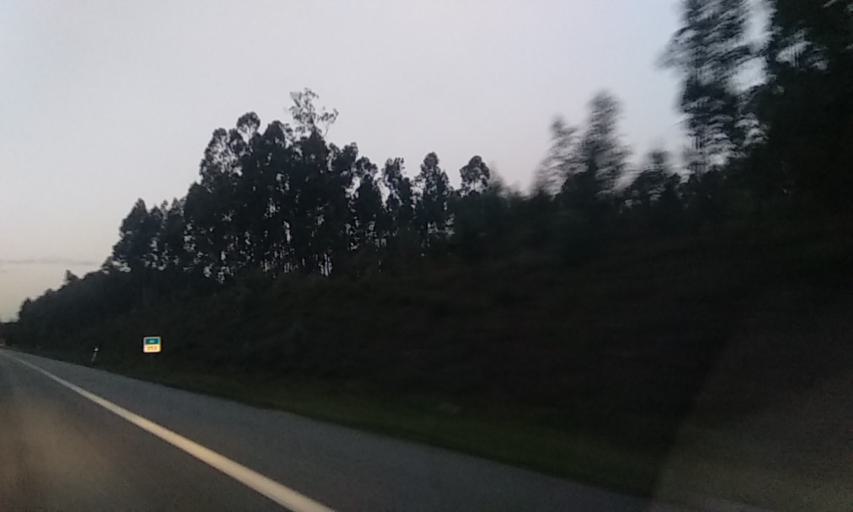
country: PT
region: Aveiro
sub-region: Estarreja
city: Salreu
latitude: 40.7394
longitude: -8.5253
